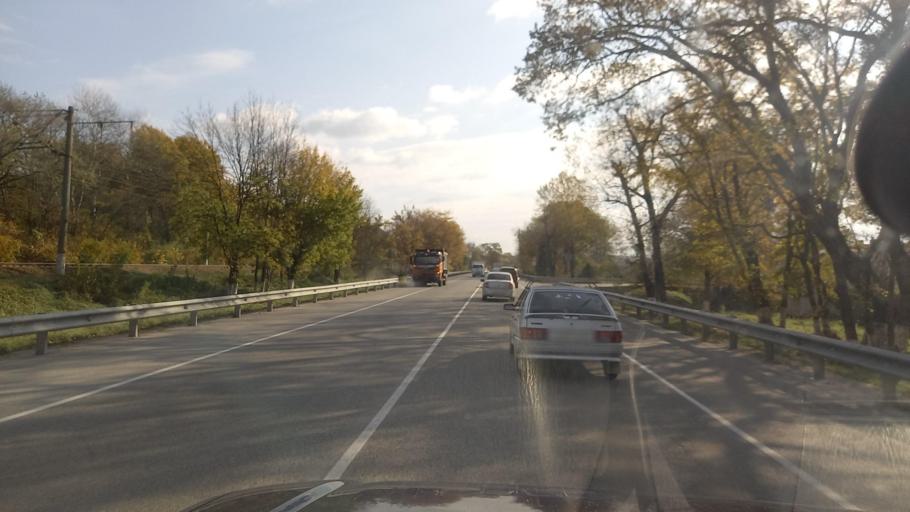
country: RU
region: Krasnodarskiy
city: Gayduk
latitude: 44.8717
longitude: 37.8380
